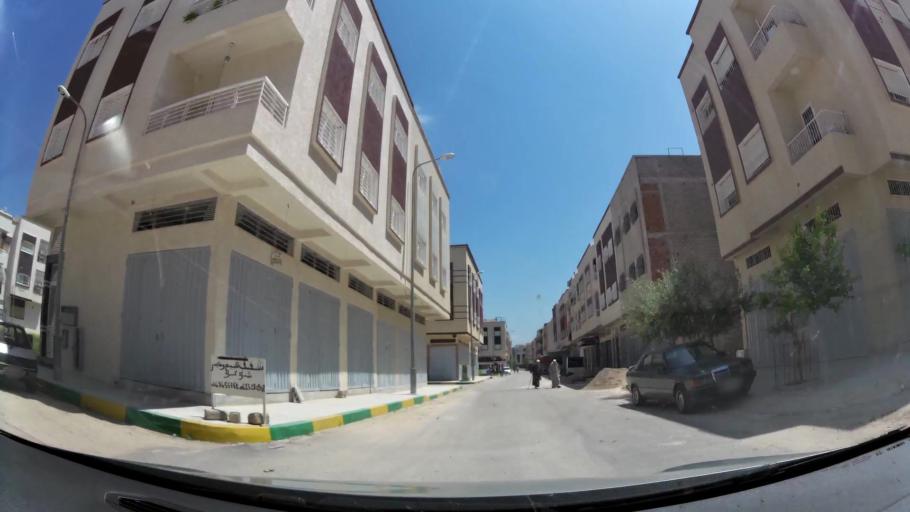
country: MA
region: Fes-Boulemane
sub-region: Fes
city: Fes
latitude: 34.0206
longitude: -5.0515
